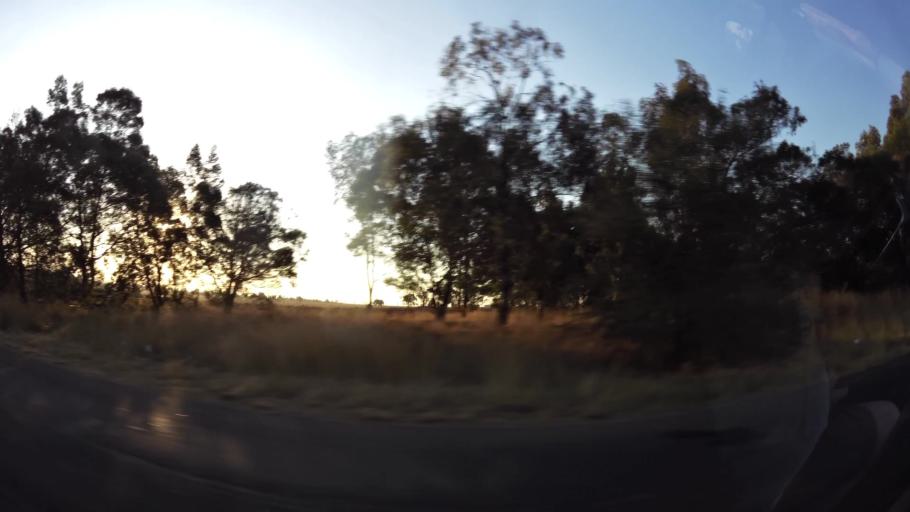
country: ZA
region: Gauteng
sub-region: West Rand District Municipality
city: Randfontein
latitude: -26.2037
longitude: 27.6672
